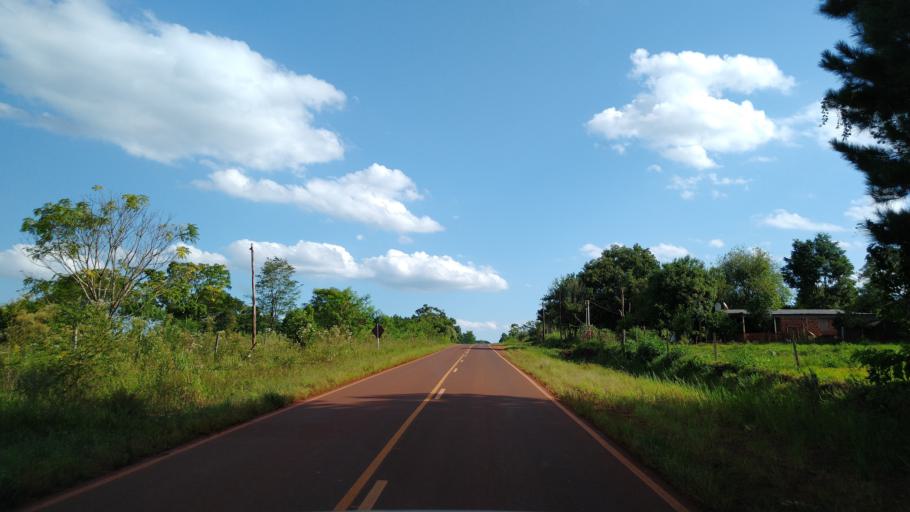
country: AR
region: Misiones
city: Puerto Piray
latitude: -26.4809
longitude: -54.6721
